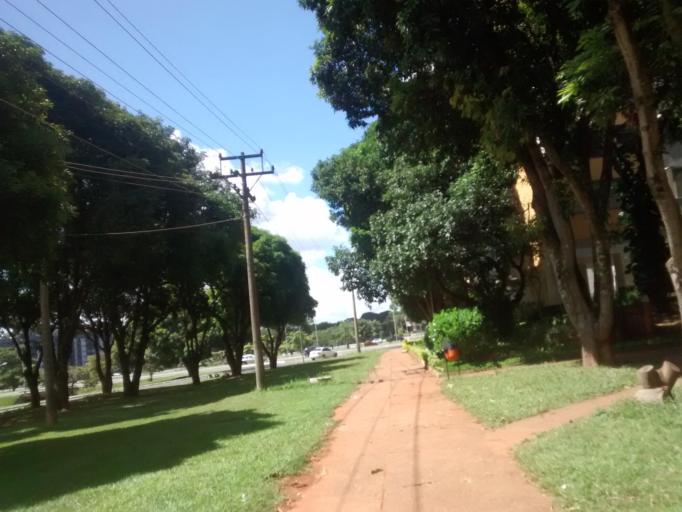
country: BR
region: Federal District
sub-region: Brasilia
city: Brasilia
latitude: -15.7529
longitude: -47.8886
